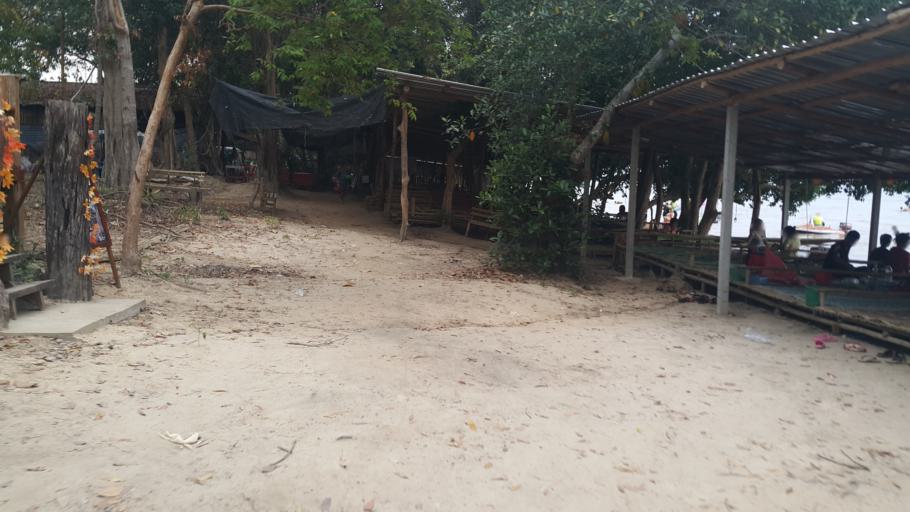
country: TH
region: Nong Khai
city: Bueng Khong Long
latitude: 17.9830
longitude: 104.0266
